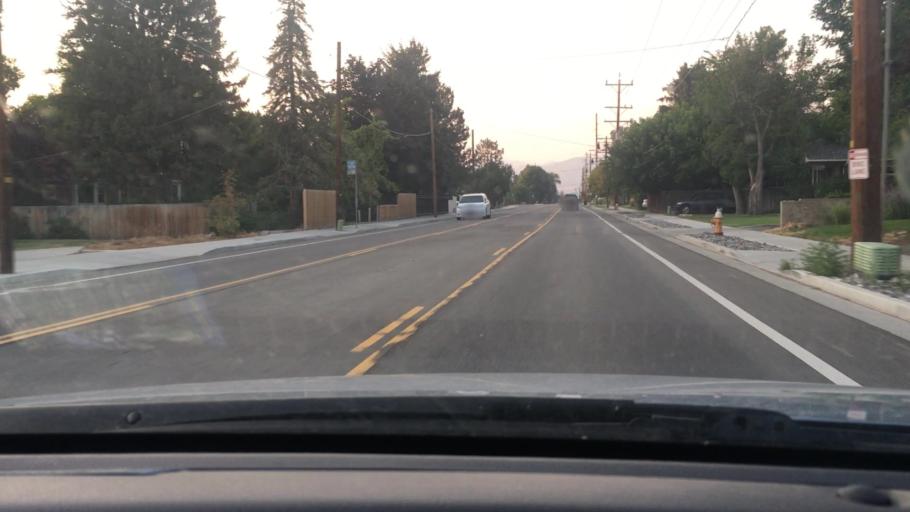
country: US
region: Utah
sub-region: Salt Lake County
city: Canyon Rim
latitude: 40.6920
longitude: -111.8244
